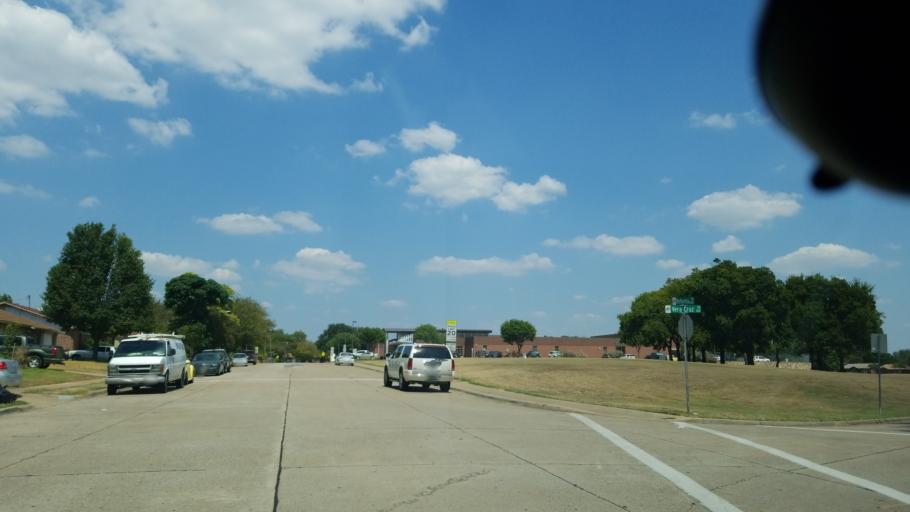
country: US
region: Texas
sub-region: Dallas County
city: Grand Prairie
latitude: 32.7004
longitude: -96.9902
